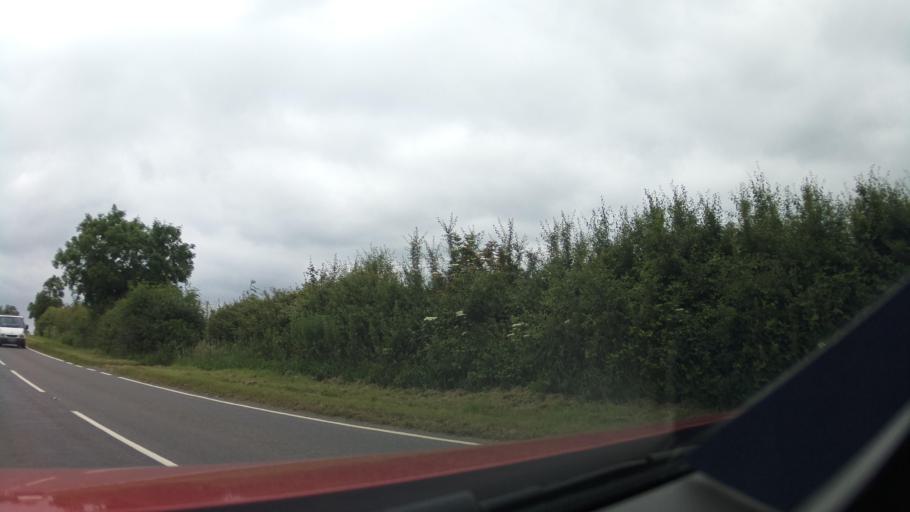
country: GB
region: England
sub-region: Leicestershire
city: Grimston
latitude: 52.7846
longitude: -1.0048
